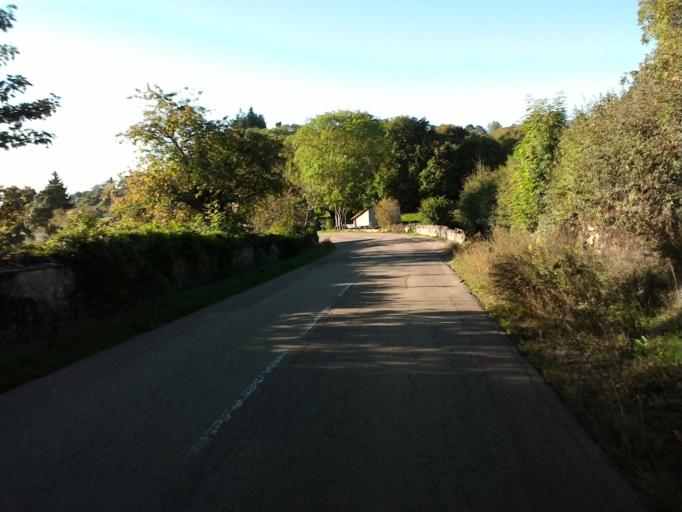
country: FR
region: Bourgogne
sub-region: Departement de la Cote-d'Or
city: Saulieu
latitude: 47.2742
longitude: 4.2356
